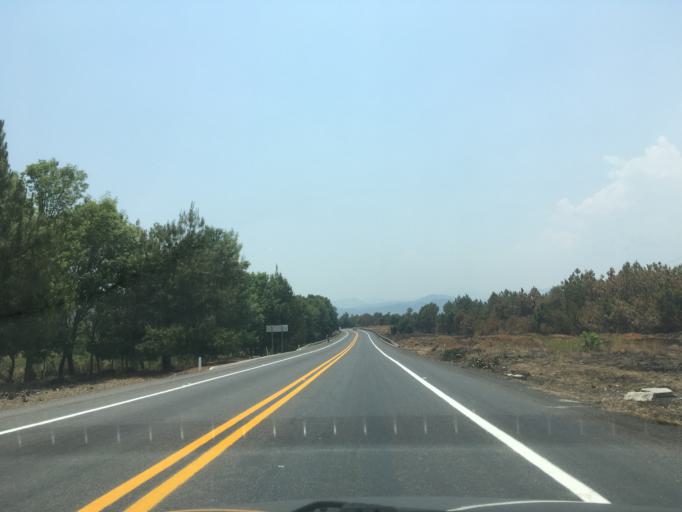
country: MX
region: Michoacan
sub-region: Patzcuaro
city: Santa Ana Chapitiro
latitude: 19.5066
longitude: -101.6644
